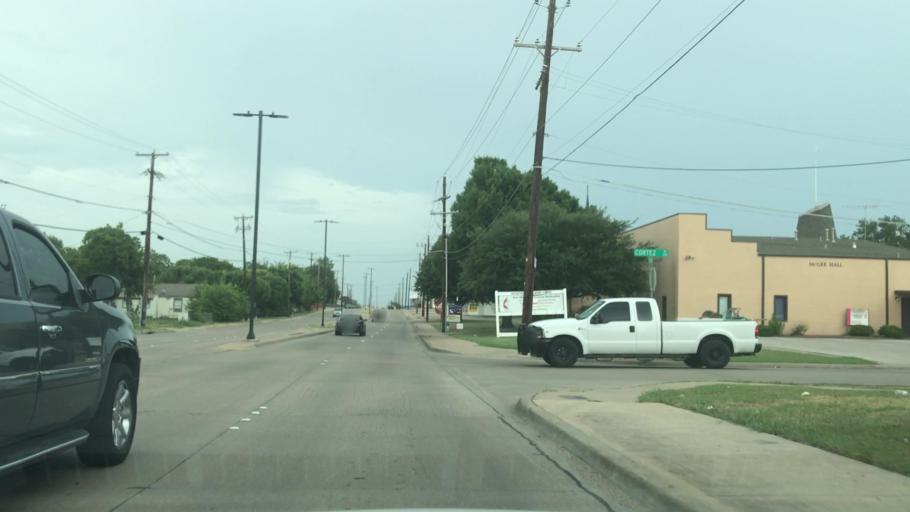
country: US
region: Texas
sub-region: Dallas County
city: Garland
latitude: 32.8788
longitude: -96.6539
